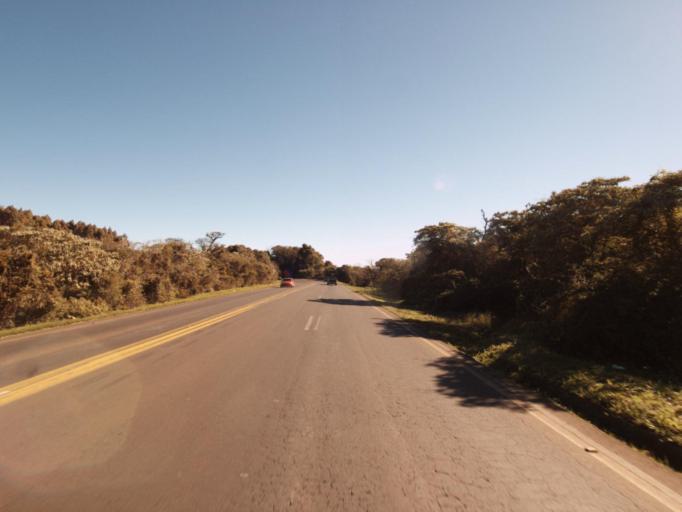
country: BR
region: Santa Catarina
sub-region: Xanxere
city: Xanxere
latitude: -26.9161
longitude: -52.4911
